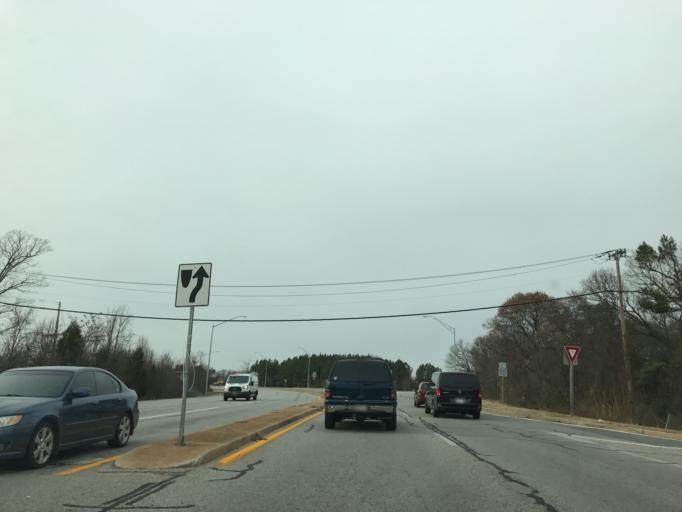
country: US
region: Maryland
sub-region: Anne Arundel County
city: Glen Burnie
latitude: 39.1563
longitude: -76.6002
